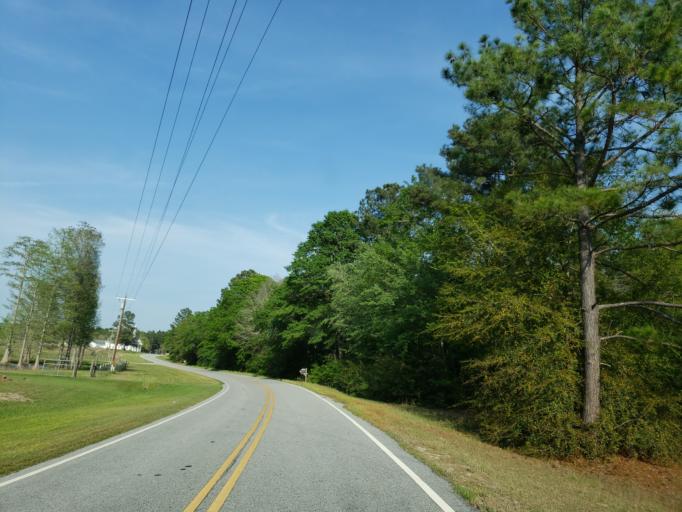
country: US
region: Georgia
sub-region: Tift County
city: Tifton
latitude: 31.5744
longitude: -83.4995
